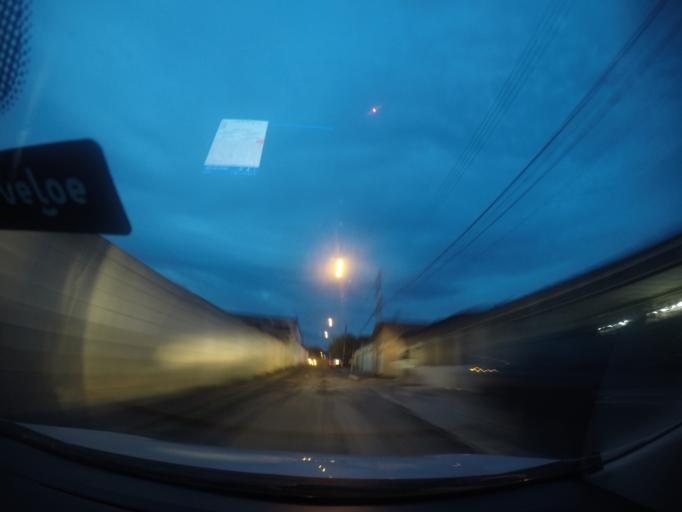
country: BR
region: Goias
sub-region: Goiania
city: Goiania
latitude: -16.6427
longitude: -49.2395
